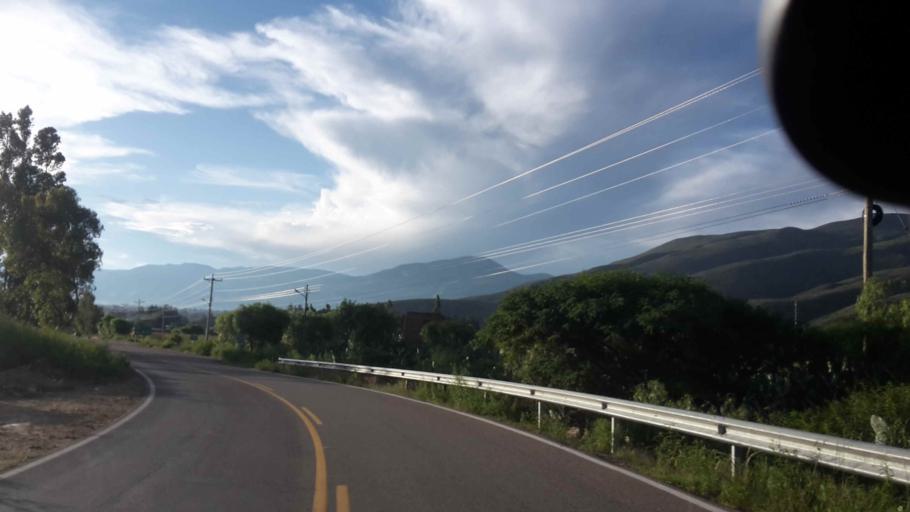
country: BO
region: Cochabamba
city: Arani
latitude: -17.5755
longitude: -65.7591
